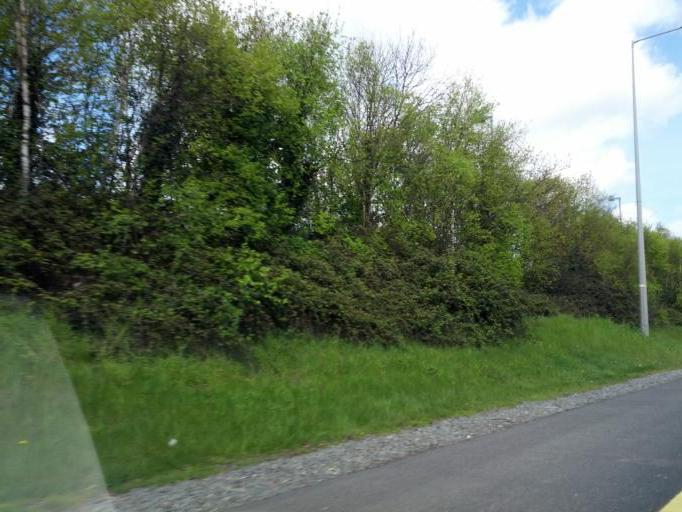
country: IE
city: Palmerstown
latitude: 53.3486
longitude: -6.3863
